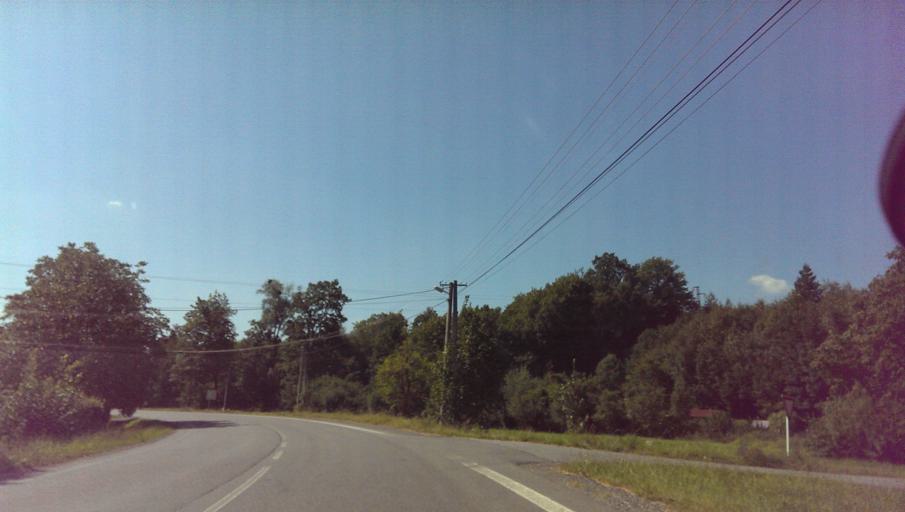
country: CZ
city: Frycovice
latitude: 49.6518
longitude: 18.2166
